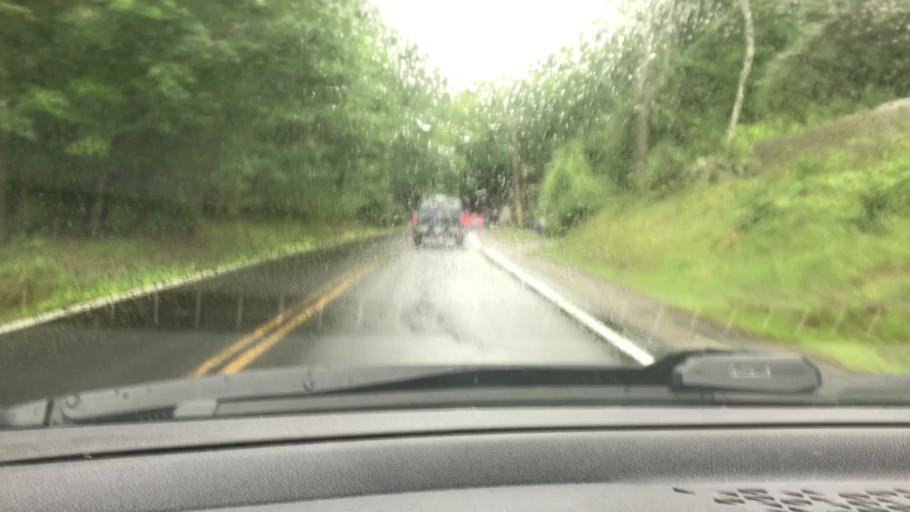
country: US
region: New Hampshire
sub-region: Merrimack County
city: Epsom
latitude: 43.1884
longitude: -71.2680
